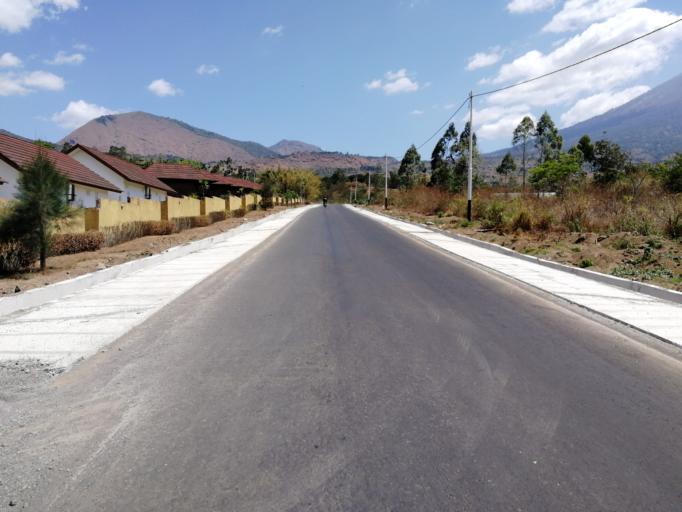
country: ID
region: West Nusa Tenggara
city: Sembalunlawang
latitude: -8.3559
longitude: 116.5139
